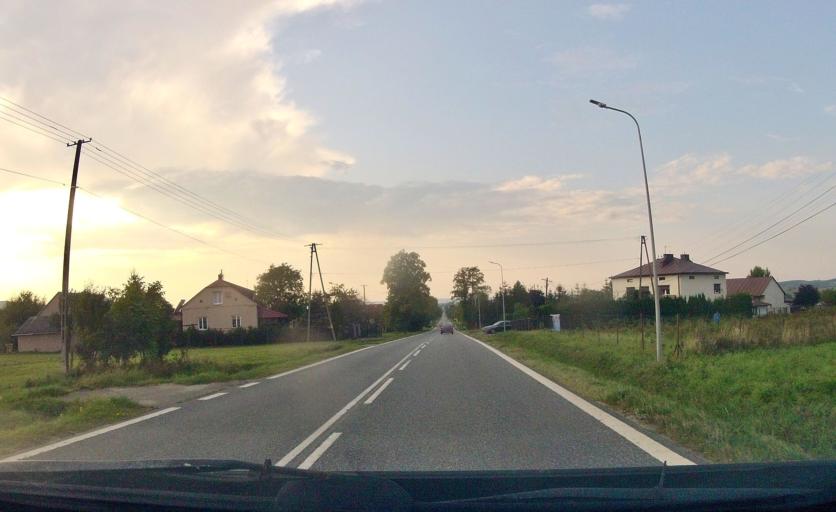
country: PL
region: Subcarpathian Voivodeship
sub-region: Powiat jasielski
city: Nowy Zmigrod
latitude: 49.5878
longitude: 21.5445
